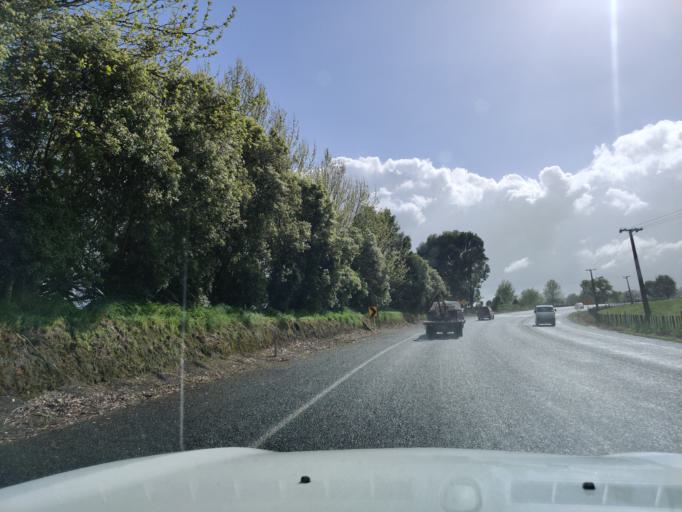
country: NZ
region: Waikato
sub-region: Matamata-Piako District
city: Matamata
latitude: -37.9440
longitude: 175.6585
